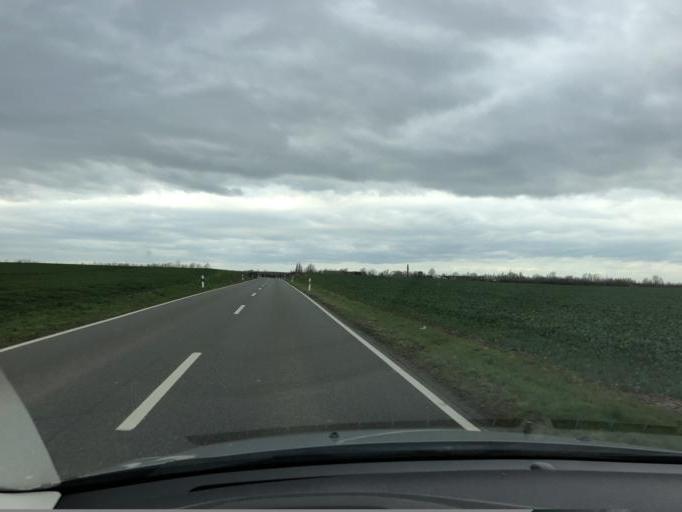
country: DE
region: Saxony-Anhalt
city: Hohenmolsen
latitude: 51.1436
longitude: 12.1372
